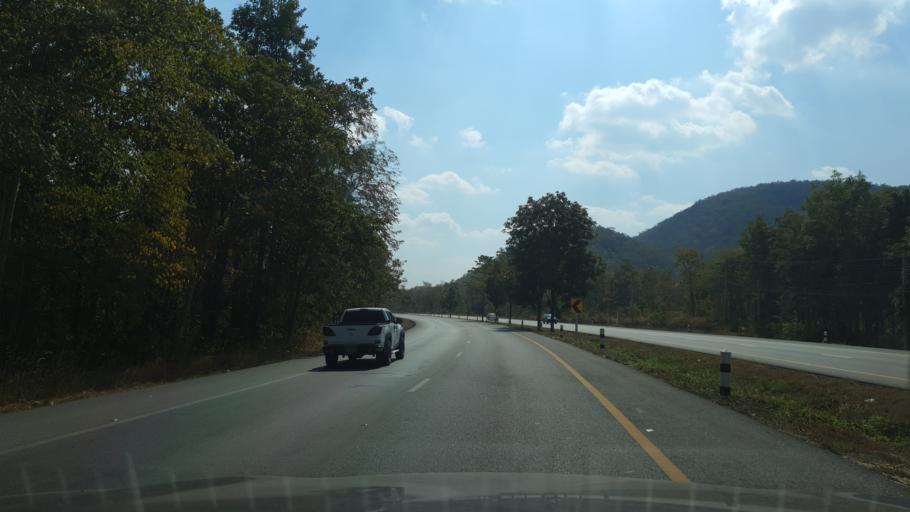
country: TH
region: Lampang
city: Mae Phrik
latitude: 17.3433
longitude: 99.1496
